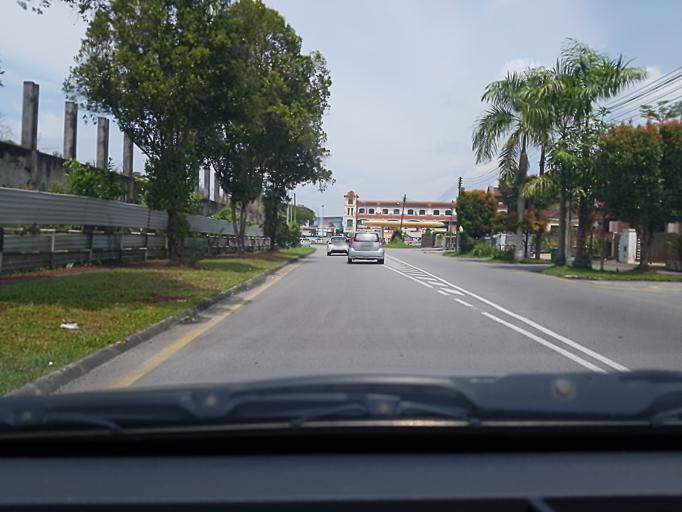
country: MY
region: Sarawak
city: Kuching
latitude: 1.5196
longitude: 110.3681
